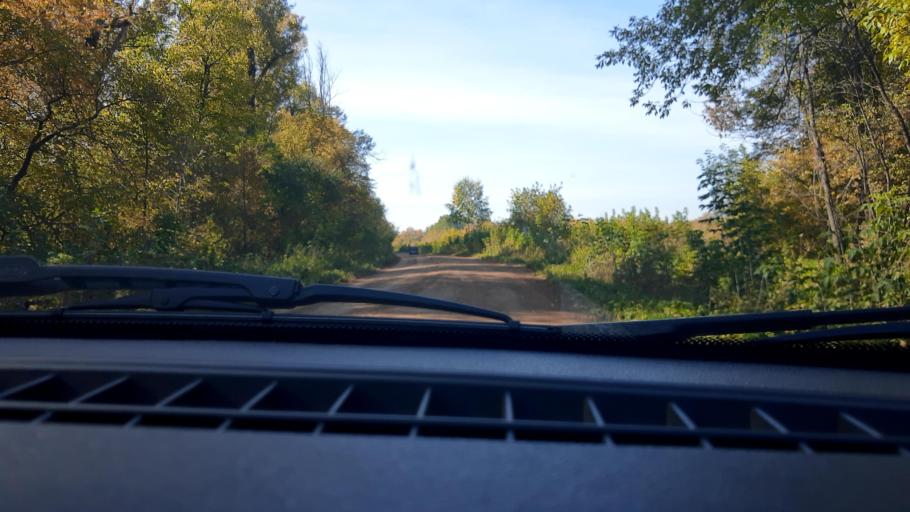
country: RU
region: Bashkortostan
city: Mikhaylovka
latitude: 54.7477
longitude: 55.8685
